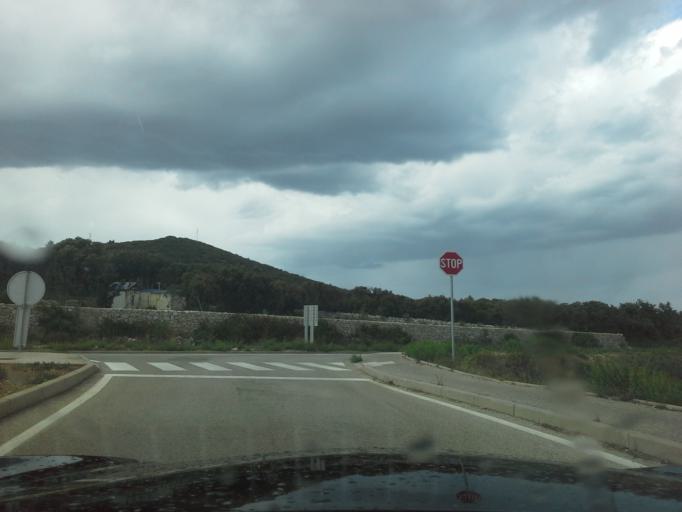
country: HR
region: Primorsko-Goranska
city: Mali Losinj
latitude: 44.6677
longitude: 14.3970
